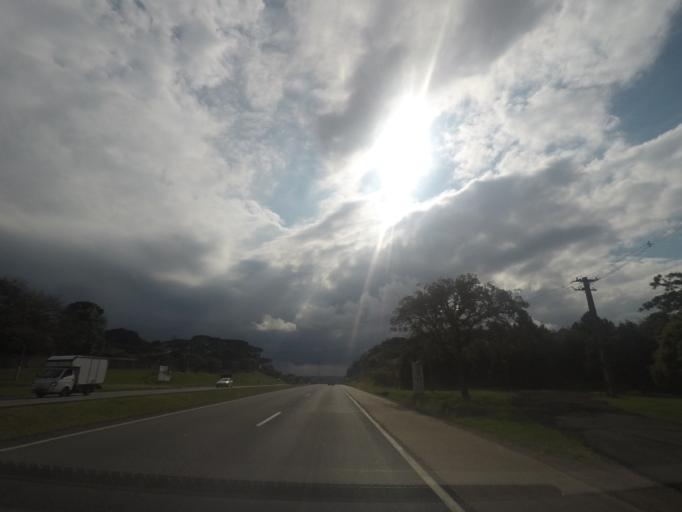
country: BR
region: Parana
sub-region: Sao Jose Dos Pinhais
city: Sao Jose dos Pinhais
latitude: -25.5060
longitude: -49.1402
